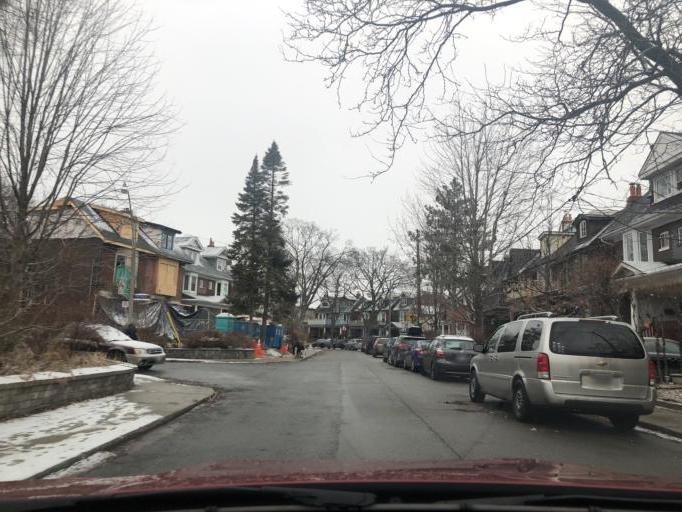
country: CA
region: Ontario
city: Toronto
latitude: 43.6780
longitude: -79.3379
